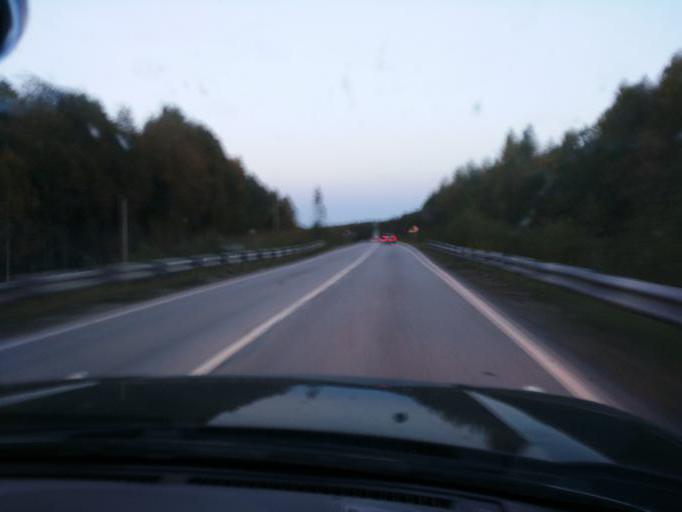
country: RU
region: Perm
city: Verkhnechusovskiye Gorodki
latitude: 58.2470
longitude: 57.0219
